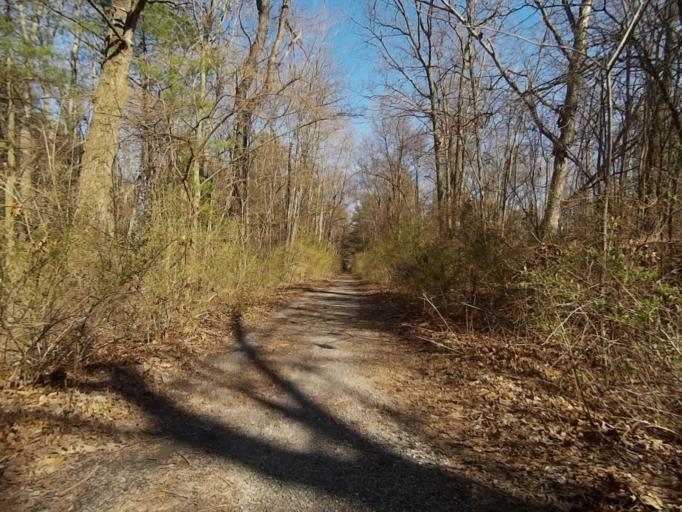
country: US
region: Pennsylvania
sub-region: Centre County
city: Park Forest Village
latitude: 40.8247
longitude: -77.9072
